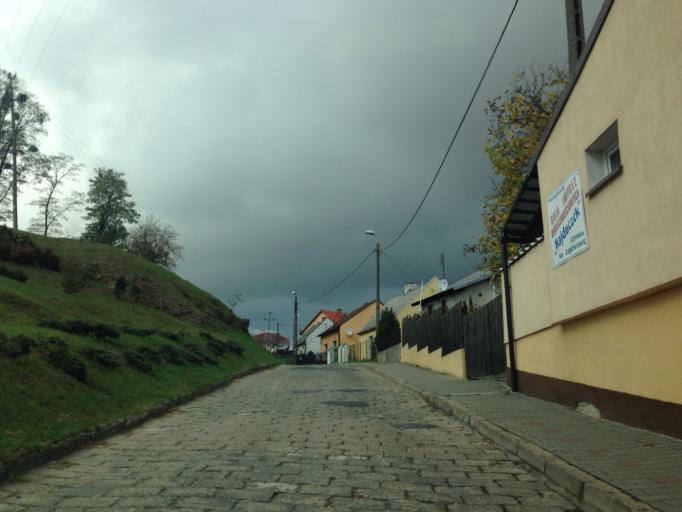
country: PL
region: Kujawsko-Pomorskie
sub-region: Powiat brodnicki
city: Gorzno
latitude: 53.1989
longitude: 19.6408
